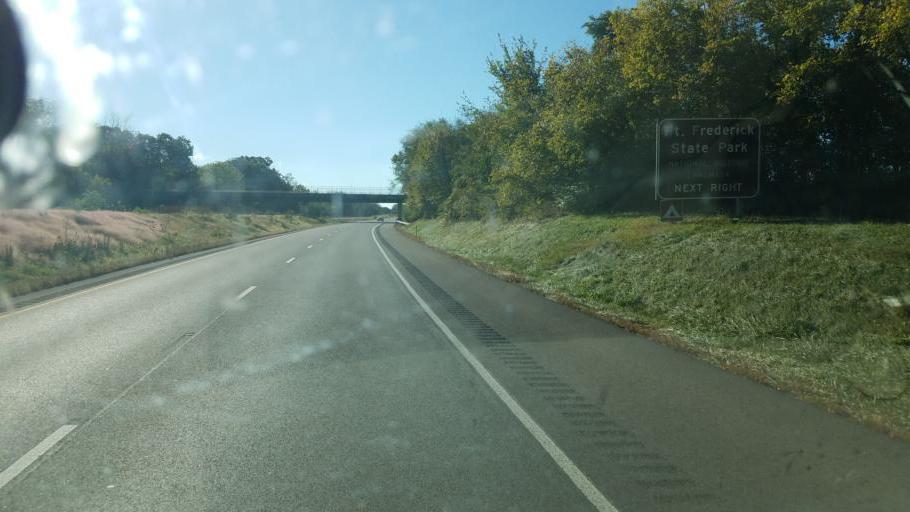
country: US
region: Maryland
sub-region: Washington County
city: Hancock
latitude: 39.6387
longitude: -78.0282
